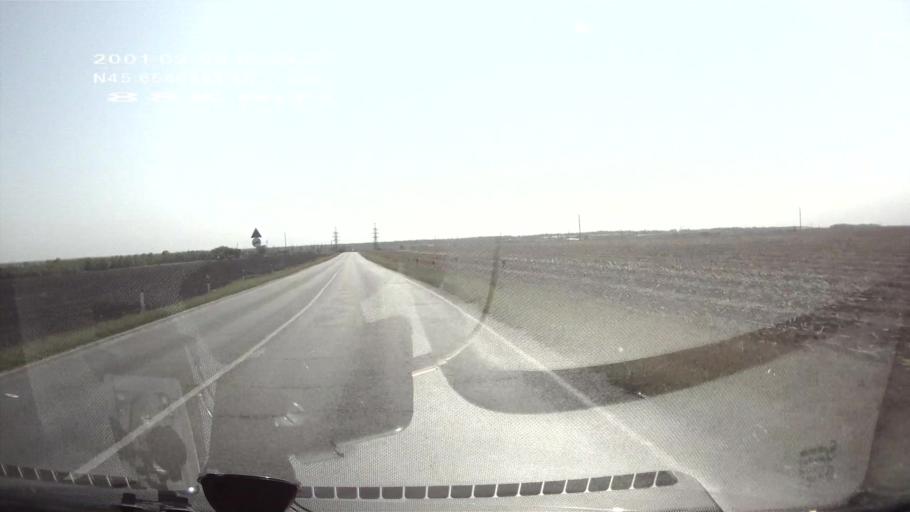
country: RU
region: Krasnodarskiy
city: Dmitriyevskaya
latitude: 45.6638
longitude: 40.7452
